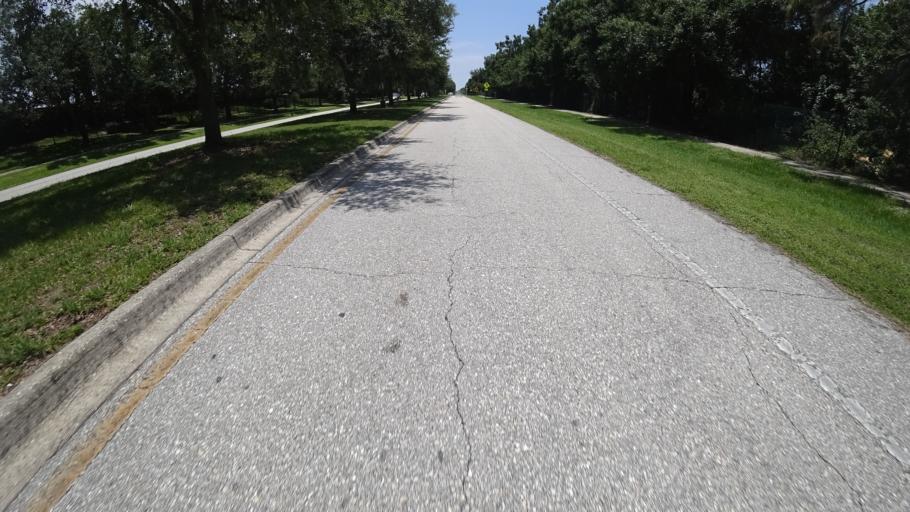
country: US
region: Florida
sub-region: Sarasota County
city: The Meadows
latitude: 27.4010
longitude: -82.4632
